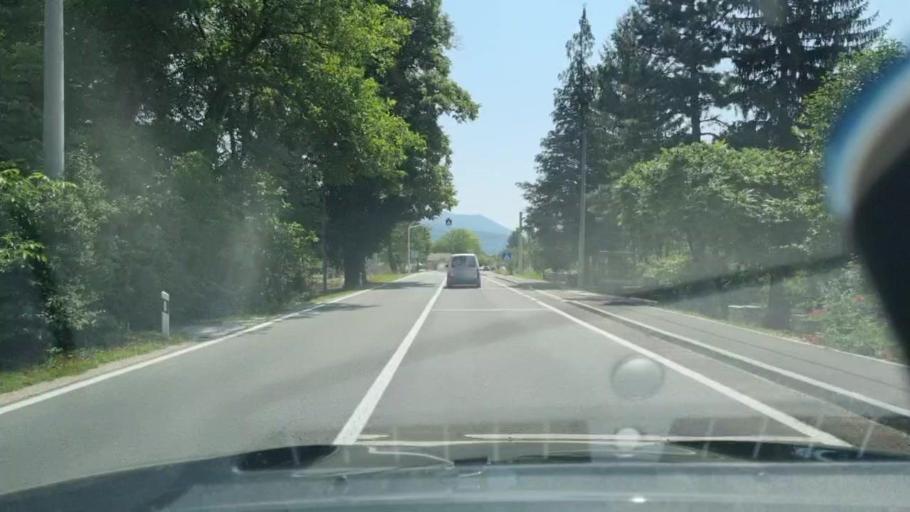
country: BA
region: Federation of Bosnia and Herzegovina
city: Bihac
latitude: 44.7931
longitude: 15.9251
